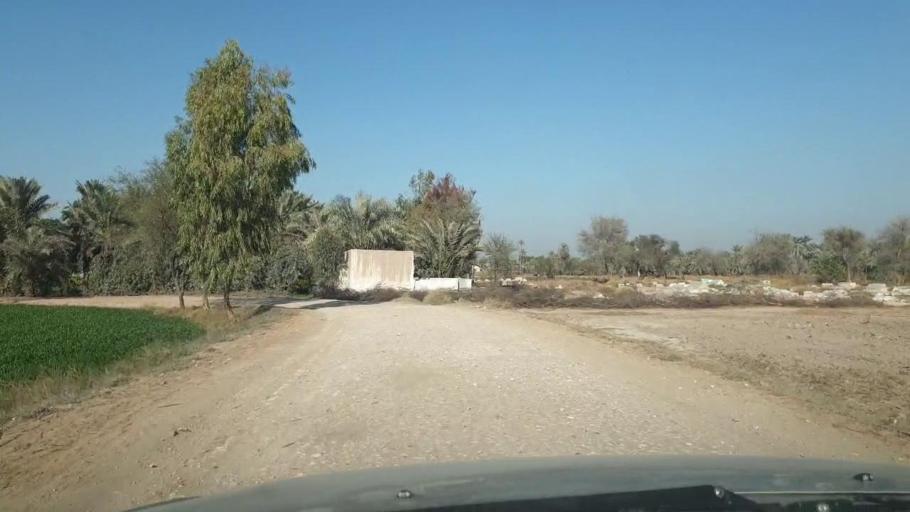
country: PK
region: Sindh
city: Ghotki
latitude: 28.0567
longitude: 69.3395
